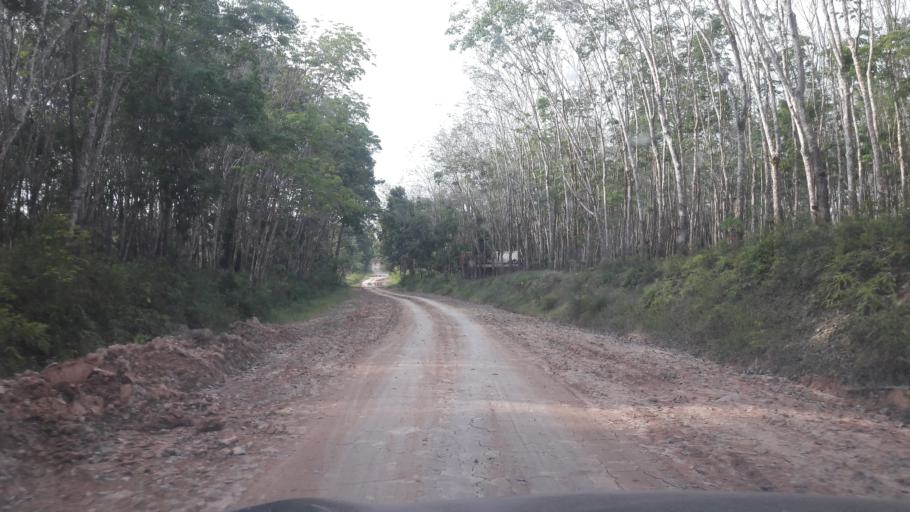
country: ID
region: South Sumatra
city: Gunungmenang
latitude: -3.2610
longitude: 103.9902
